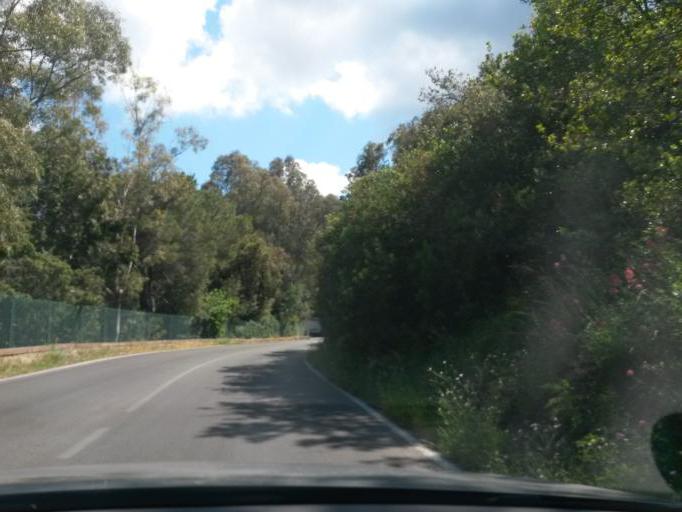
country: IT
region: Tuscany
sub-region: Provincia di Livorno
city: Marciana Marina
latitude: 42.7997
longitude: 10.2119
